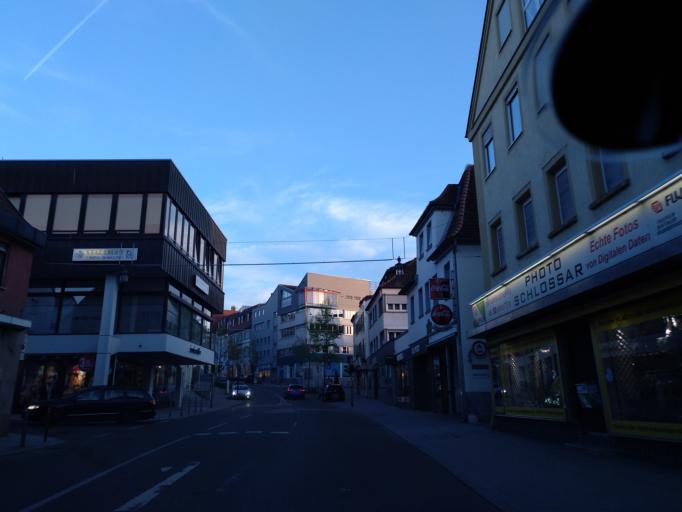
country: DE
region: Baden-Wuerttemberg
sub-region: Regierungsbezirk Stuttgart
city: Crailsheim
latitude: 49.1386
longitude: 10.0702
